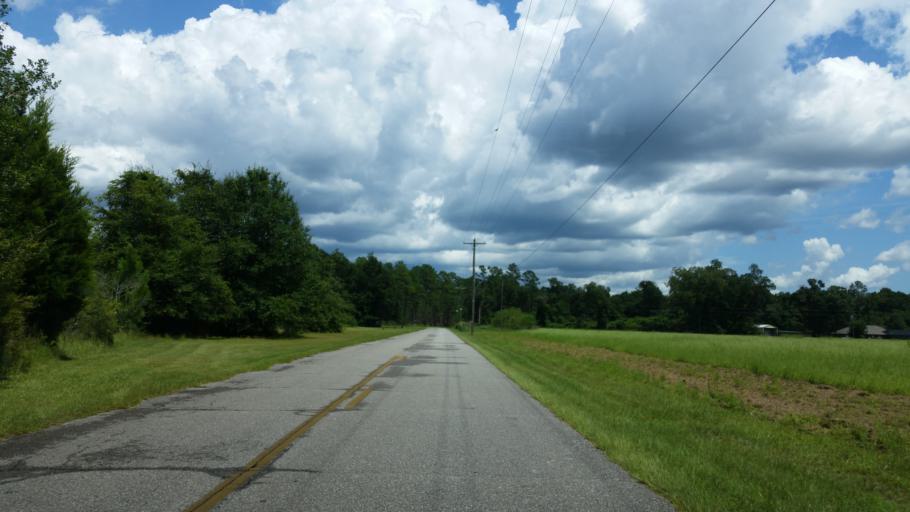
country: US
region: Florida
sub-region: Santa Rosa County
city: East Milton
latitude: 30.7340
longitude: -86.8116
